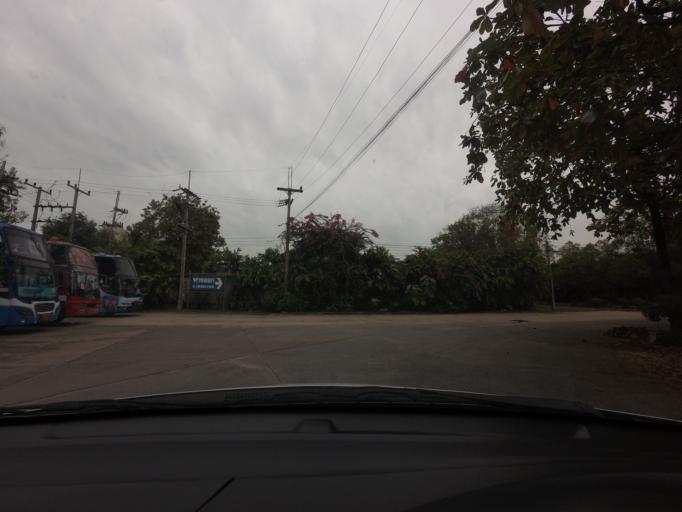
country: TH
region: Nakhon Pathom
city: Sam Phran
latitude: 13.7213
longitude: 100.2543
